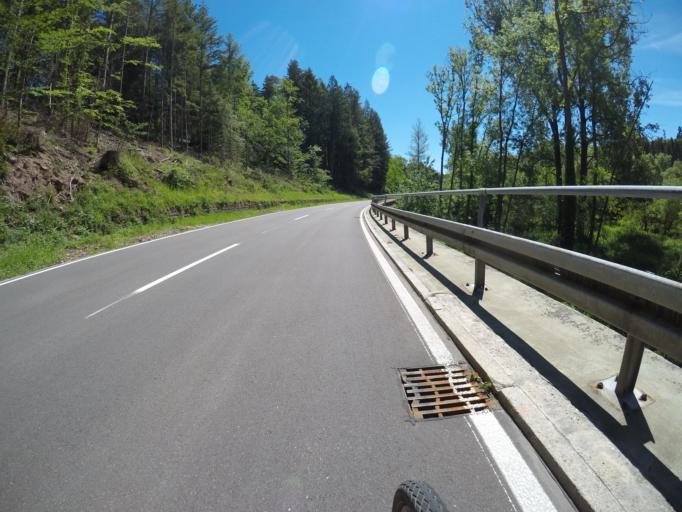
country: DE
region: Baden-Wuerttemberg
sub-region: Karlsruhe Region
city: Neuhausen
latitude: 48.8073
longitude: 8.8102
